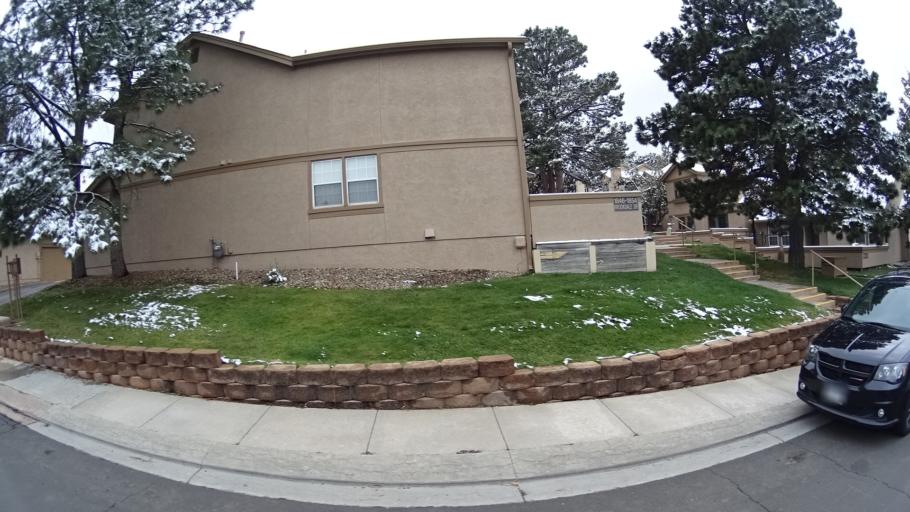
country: US
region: Colorado
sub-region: El Paso County
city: Colorado Springs
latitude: 38.9201
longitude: -104.7915
